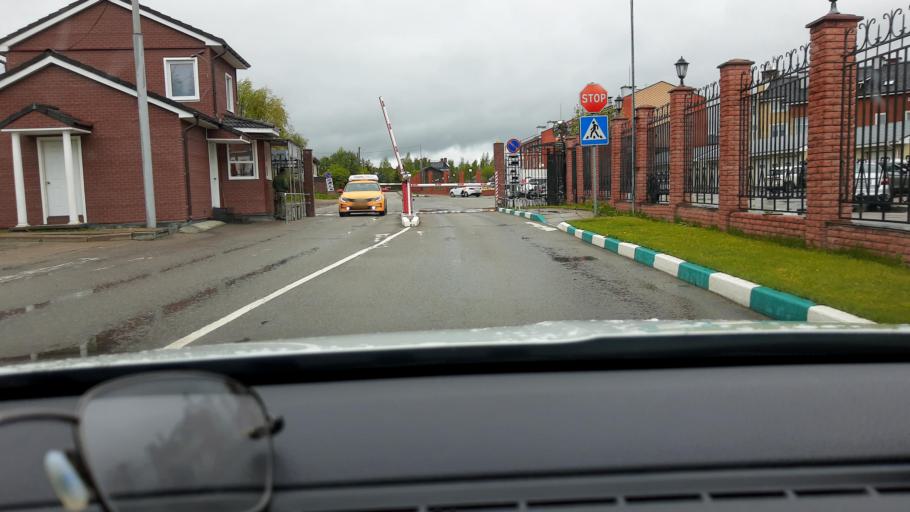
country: RU
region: Moskovskaya
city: Krasnogorsk
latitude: 55.8585
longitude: 37.3169
